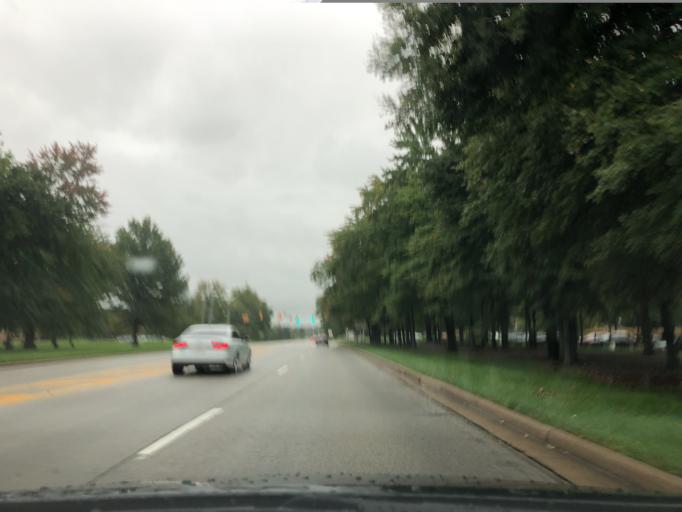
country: US
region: Ohio
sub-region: Hamilton County
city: Blue Ash
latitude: 39.2560
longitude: -84.3803
